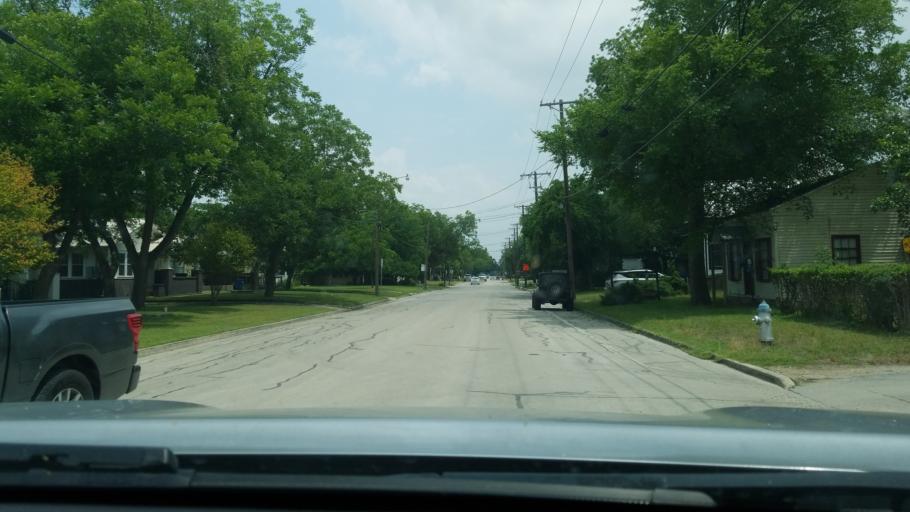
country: US
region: Texas
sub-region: Comal County
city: New Braunfels
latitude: 29.7030
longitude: -98.1223
